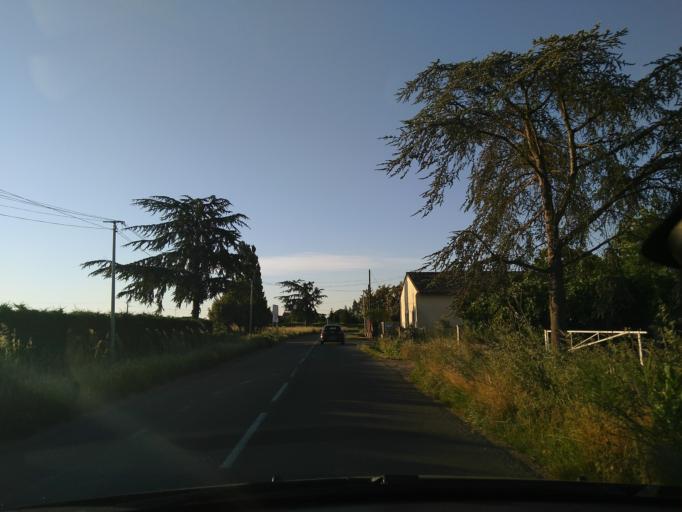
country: FR
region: Midi-Pyrenees
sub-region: Departement de la Haute-Garonne
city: Merville
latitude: 43.7119
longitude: 1.3095
